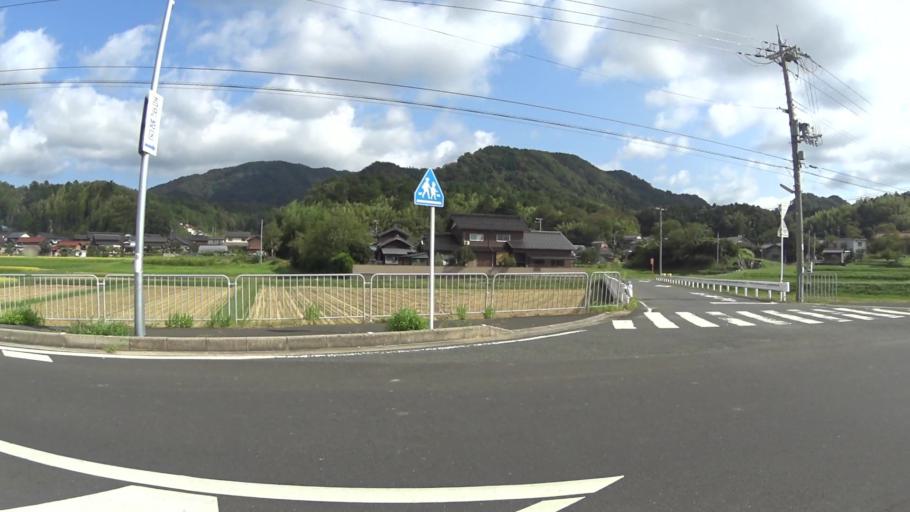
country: JP
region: Kyoto
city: Miyazu
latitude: 35.6432
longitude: 135.0884
